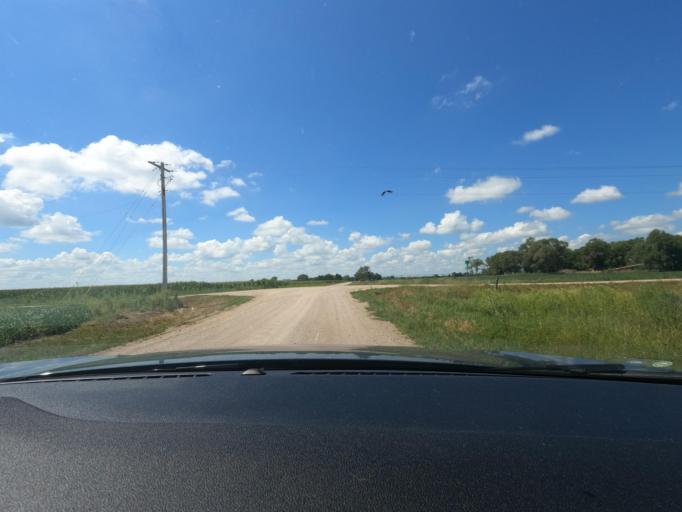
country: US
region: Nebraska
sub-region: Saunders County
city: Wahoo
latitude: 41.2491
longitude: -96.5634
